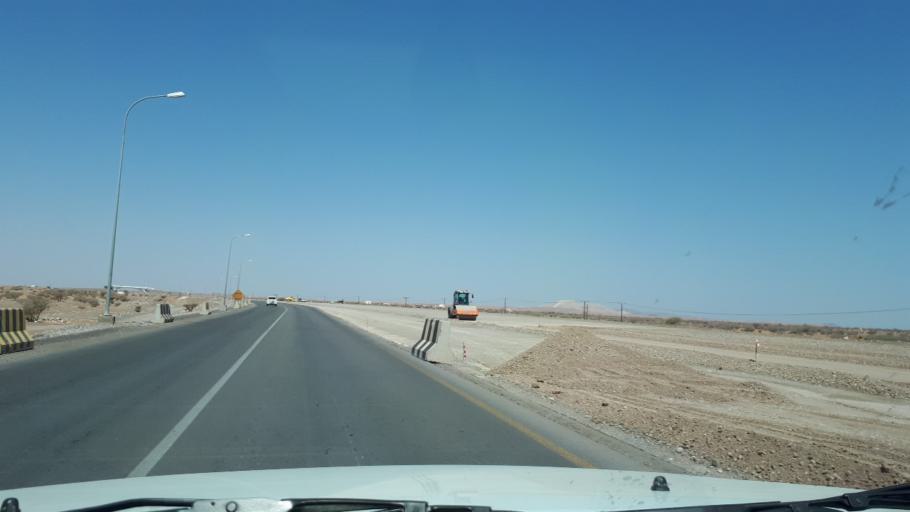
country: OM
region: Ash Sharqiyah
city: Badiyah
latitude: 22.4956
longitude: 58.9594
